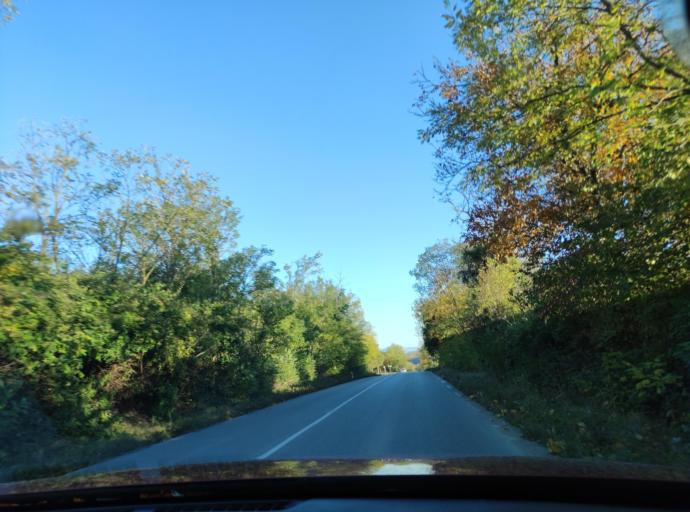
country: BG
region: Montana
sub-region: Obshtina Montana
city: Montana
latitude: 43.3979
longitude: 23.1111
